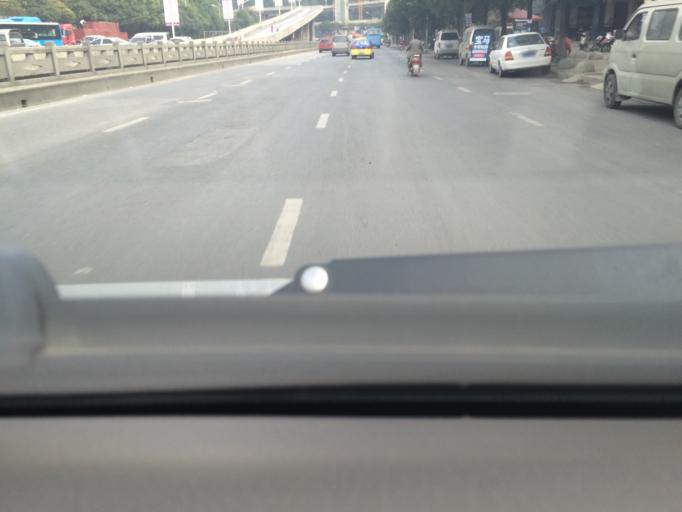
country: CN
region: Guizhou Sheng
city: Guiyang
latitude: 26.5843
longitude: 106.6786
